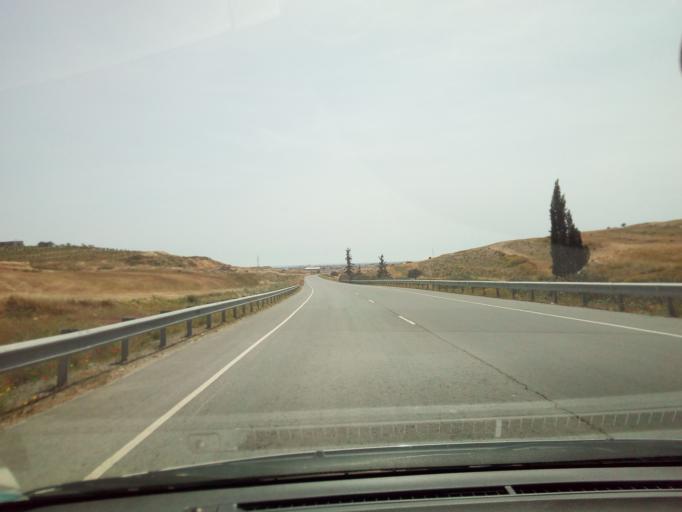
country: CY
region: Larnaka
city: Aradippou
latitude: 34.9858
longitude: 33.5775
